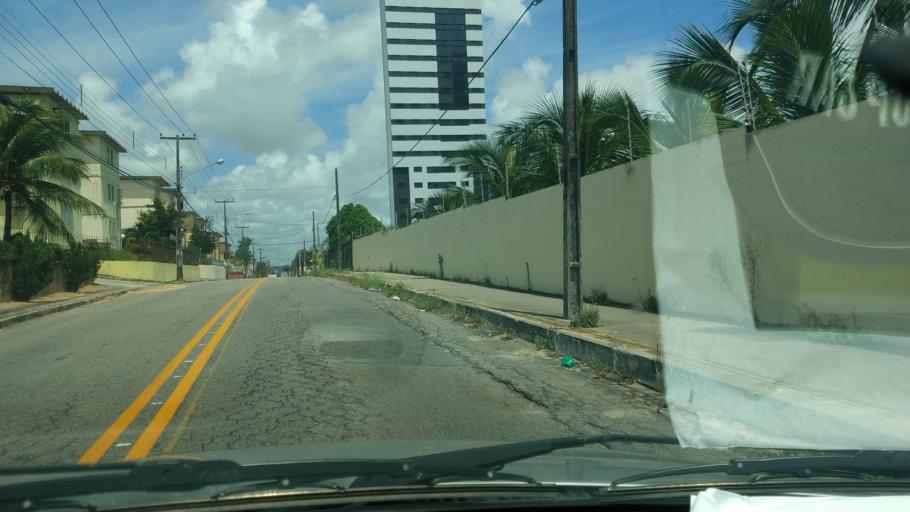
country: BR
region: Rio Grande do Norte
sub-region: Natal
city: Natal
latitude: -5.8642
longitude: -35.2008
